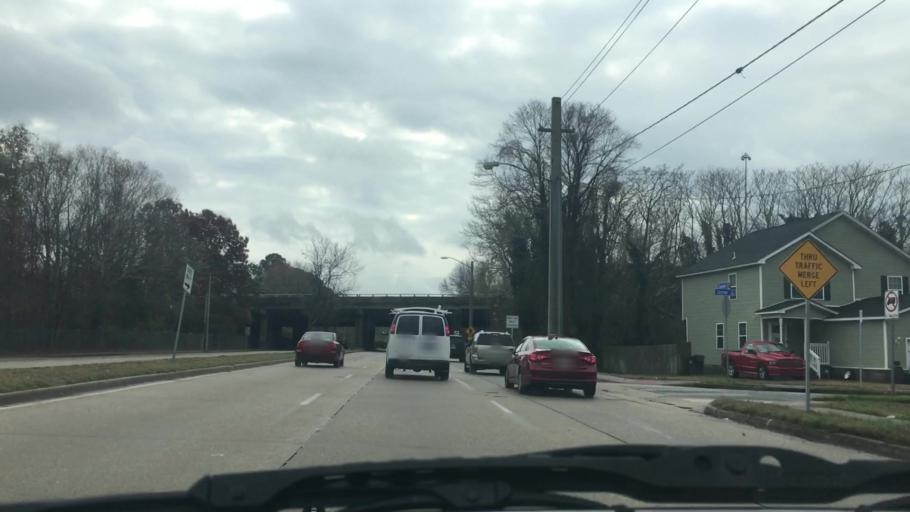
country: US
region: Virginia
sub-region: City of Norfolk
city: Norfolk
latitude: 36.9045
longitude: -76.2399
